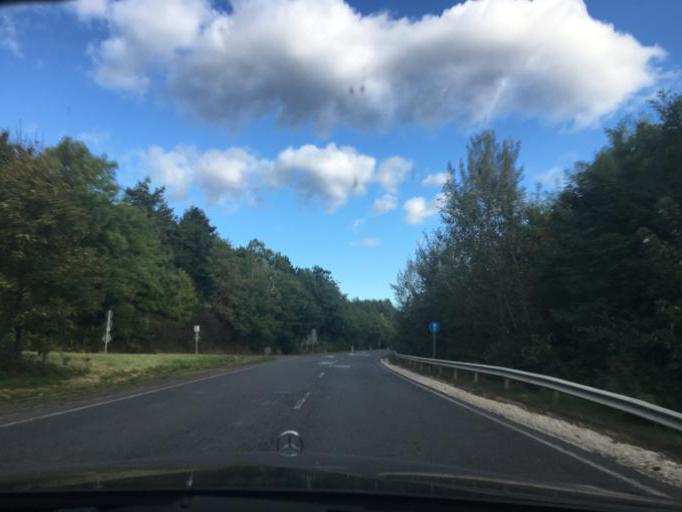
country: HU
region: Borsod-Abauj-Zemplen
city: Gonc
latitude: 48.4302
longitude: 21.1818
